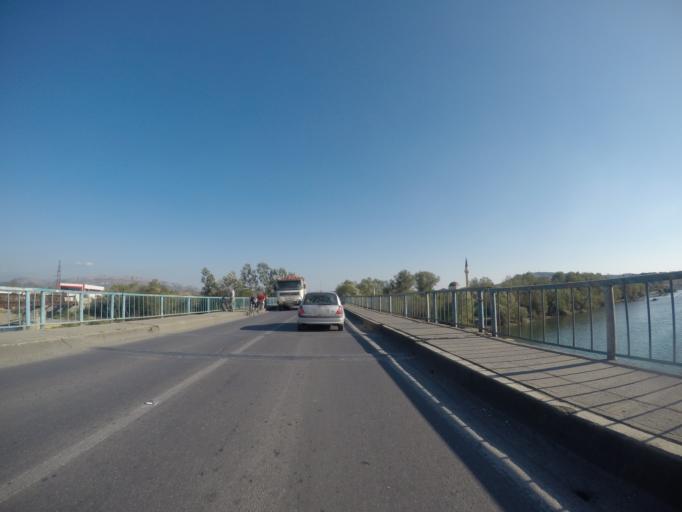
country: AL
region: Shkoder
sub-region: Rrethi i Shkodres
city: Berdica e Madhe
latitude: 42.0422
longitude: 19.4923
